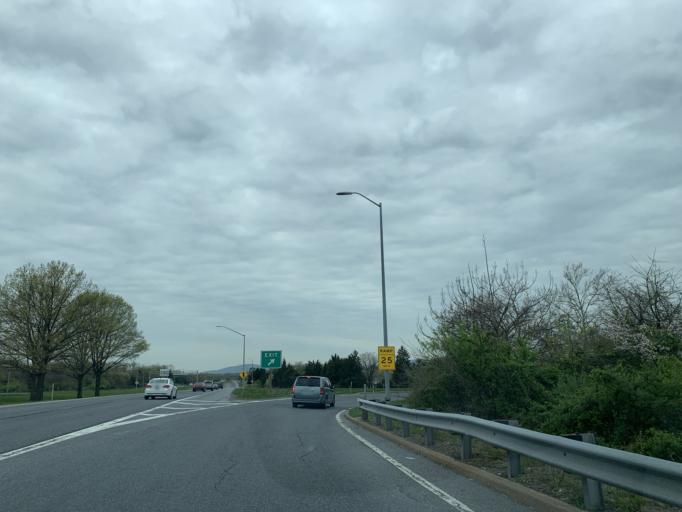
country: US
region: Maryland
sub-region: Washington County
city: Hagerstown
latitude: 39.6535
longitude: -77.7506
